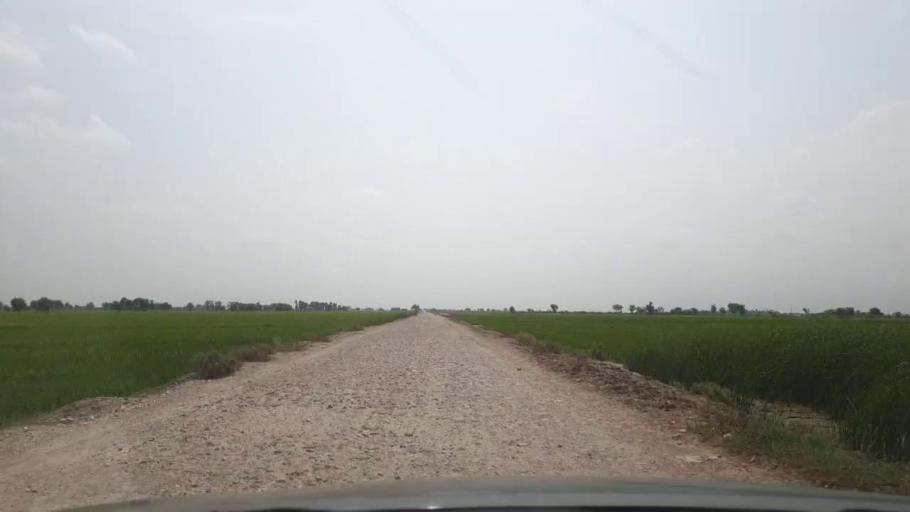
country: PK
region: Sindh
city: Ratodero
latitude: 27.8406
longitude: 68.3262
